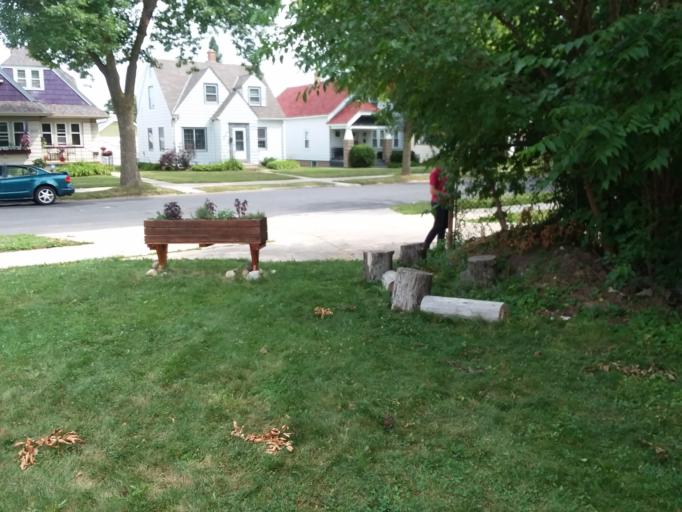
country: US
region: Wisconsin
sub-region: Milwaukee County
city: Wauwatosa
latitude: 43.0725
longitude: -87.9948
